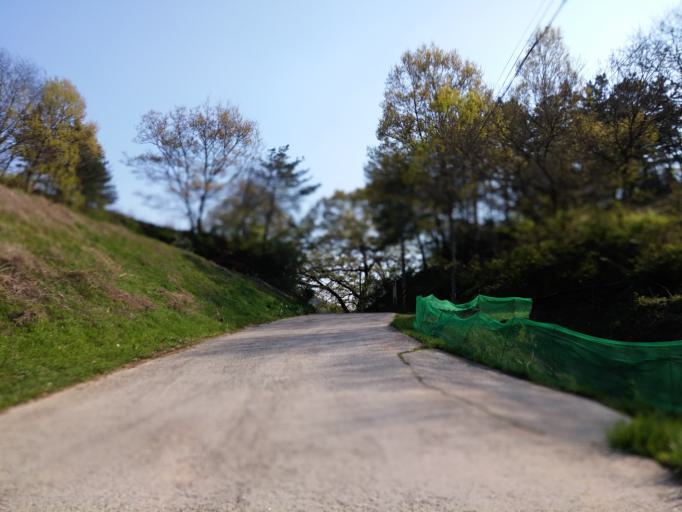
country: KR
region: Daejeon
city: Sintansin
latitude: 36.4213
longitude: 127.4823
